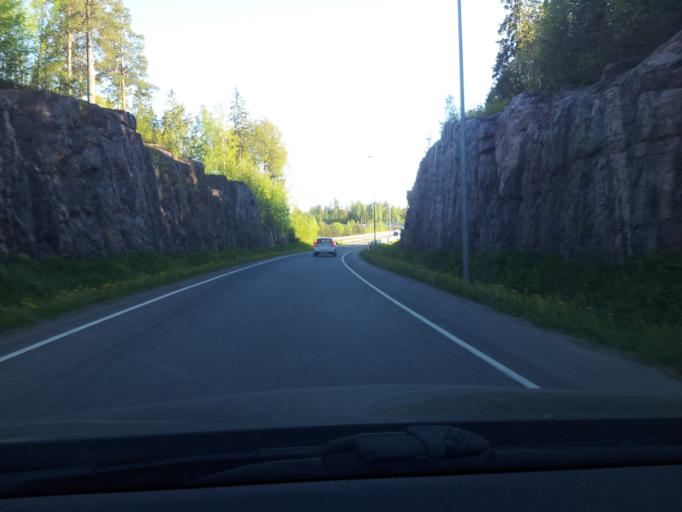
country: FI
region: Uusimaa
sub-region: Helsinki
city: Kauniainen
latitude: 60.2073
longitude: 24.7450
